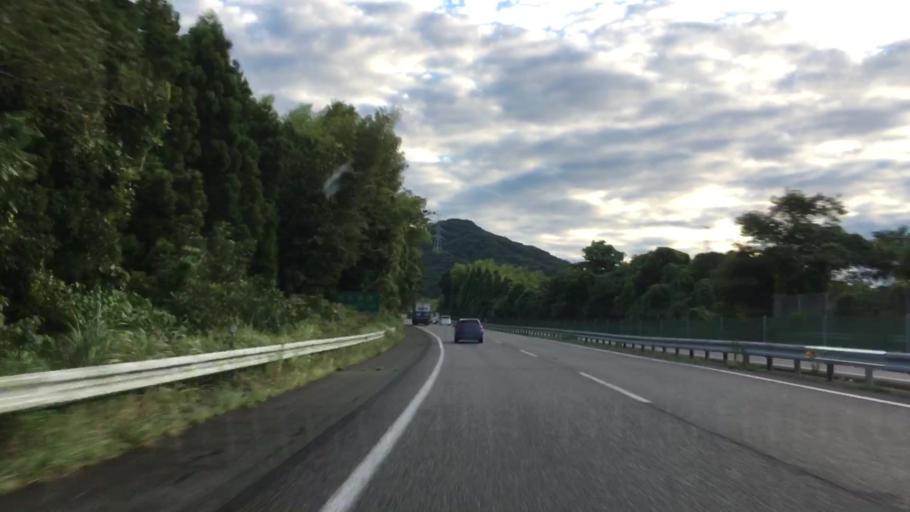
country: JP
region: Yamaguchi
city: Shimonoseki
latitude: 34.0438
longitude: 130.9879
